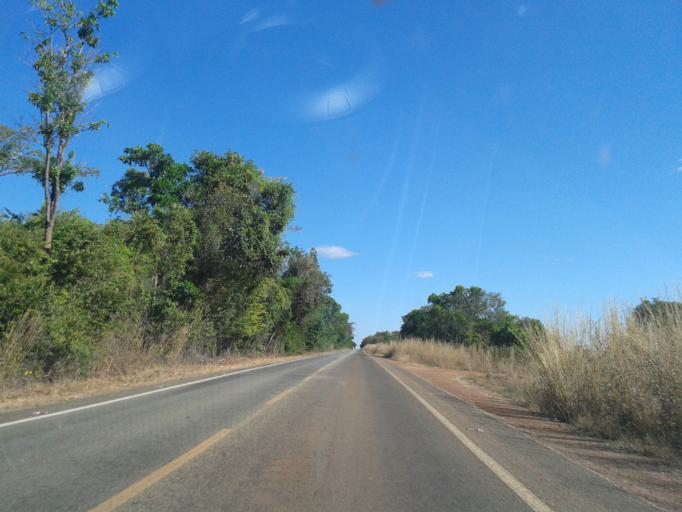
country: BR
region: Goias
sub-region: Mozarlandia
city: Mozarlandia
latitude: -14.4386
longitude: -50.4577
